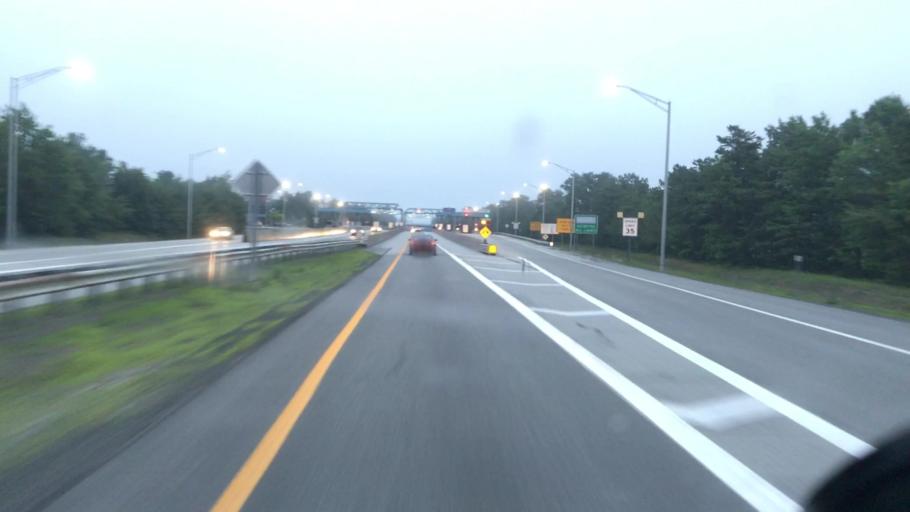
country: US
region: Maine
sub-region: Cumberland County
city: New Gloucester
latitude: 43.9334
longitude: -70.3353
